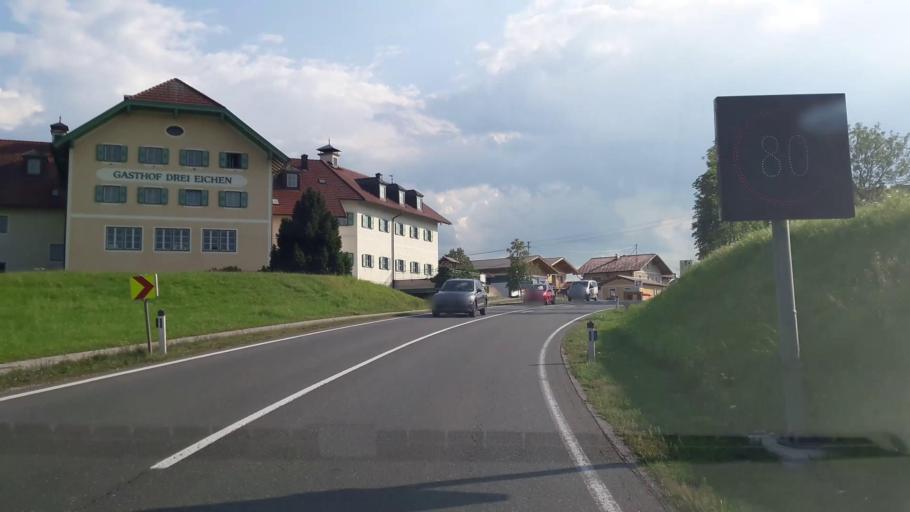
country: AT
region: Salzburg
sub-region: Politischer Bezirk Salzburg-Umgebung
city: Henndorf am Wallersee
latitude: 47.8818
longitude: 13.1724
